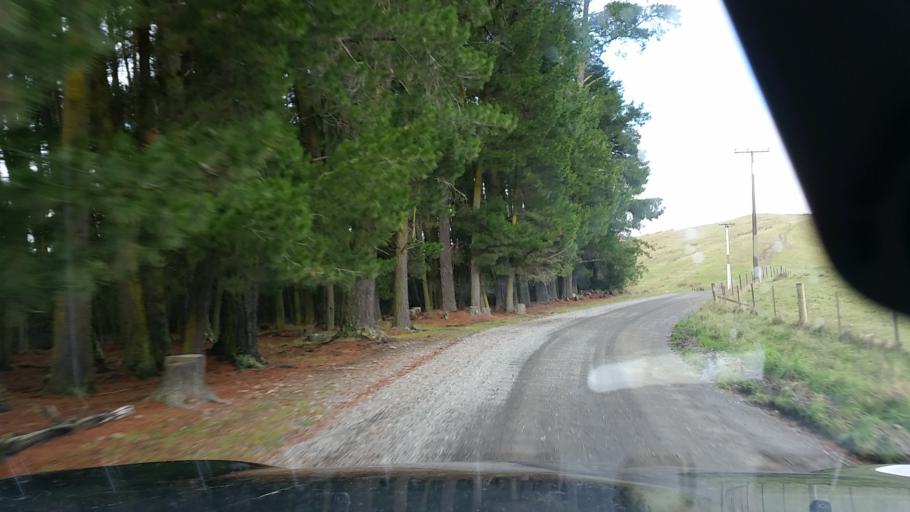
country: NZ
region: Marlborough
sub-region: Marlborough District
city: Blenheim
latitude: -41.6506
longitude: 173.6539
